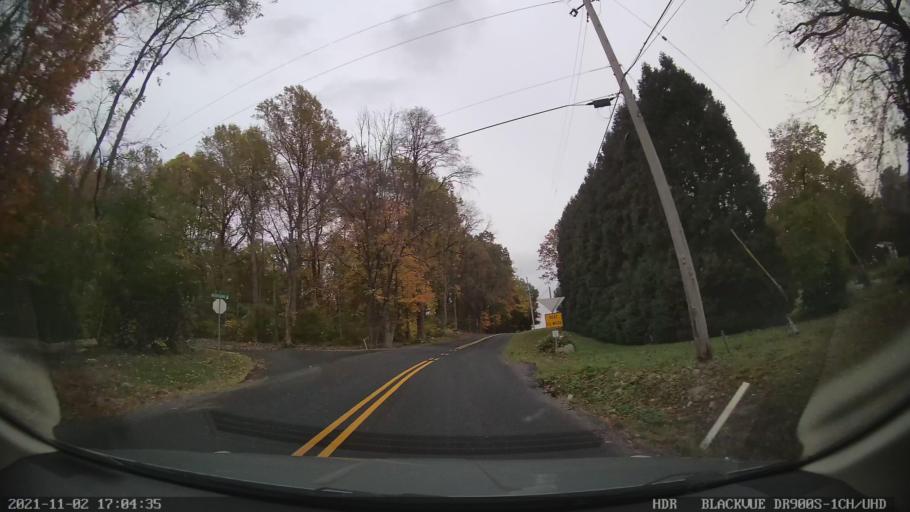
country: US
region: Pennsylvania
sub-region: Berks County
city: Fleetwood
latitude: 40.4368
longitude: -75.8367
